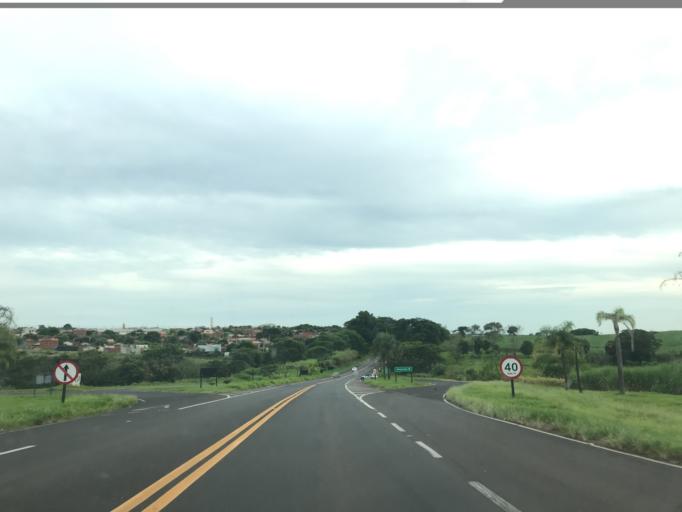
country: BR
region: Sao Paulo
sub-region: Birigui
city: Birigui
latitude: -21.5728
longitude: -50.4454
